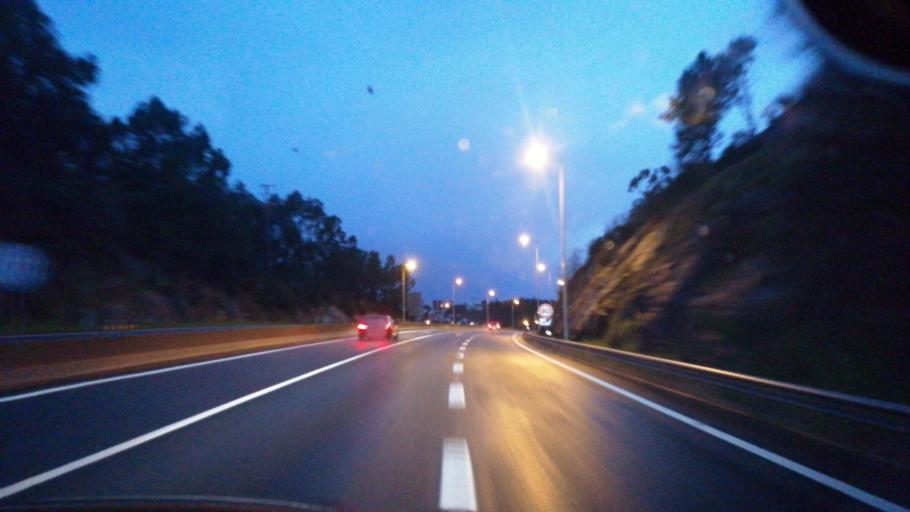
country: PT
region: Braga
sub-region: Braga
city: Oliveira
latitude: 41.5135
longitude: -8.4445
